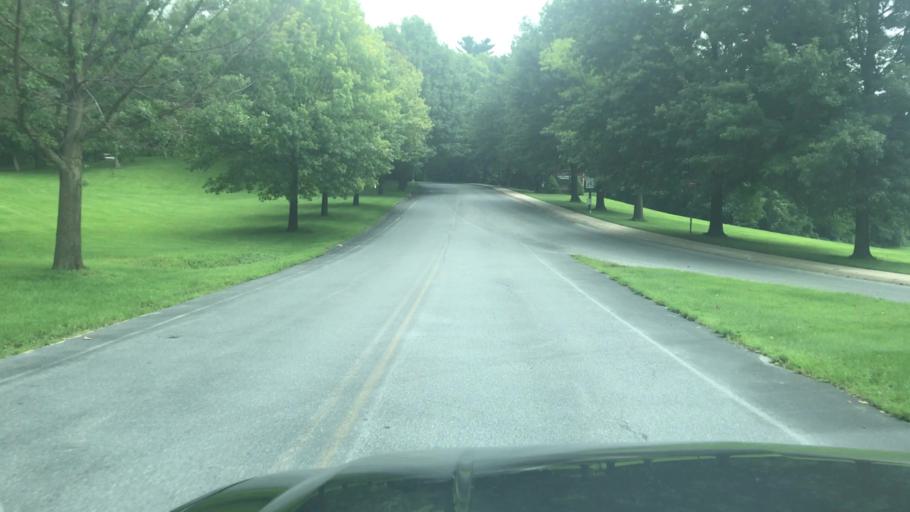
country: US
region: Pennsylvania
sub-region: Dauphin County
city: Harrisburg
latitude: 40.2861
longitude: -76.8803
